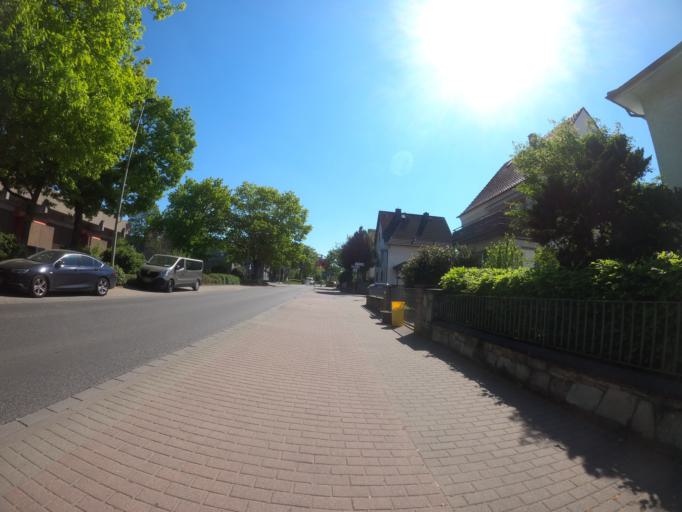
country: DE
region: Hesse
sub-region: Regierungsbezirk Darmstadt
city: Florsheim
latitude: 50.0142
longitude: 8.4214
